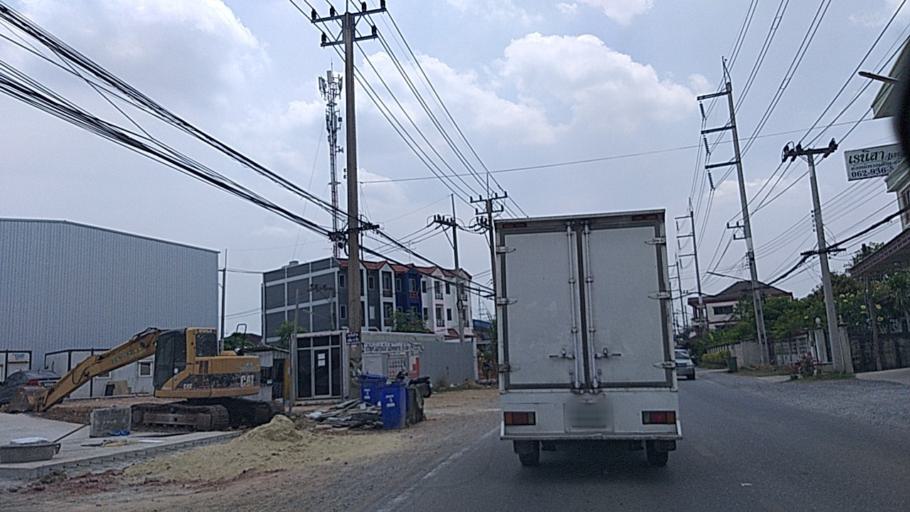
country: TH
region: Nakhon Pathom
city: Salaya
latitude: 13.7553
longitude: 100.2823
